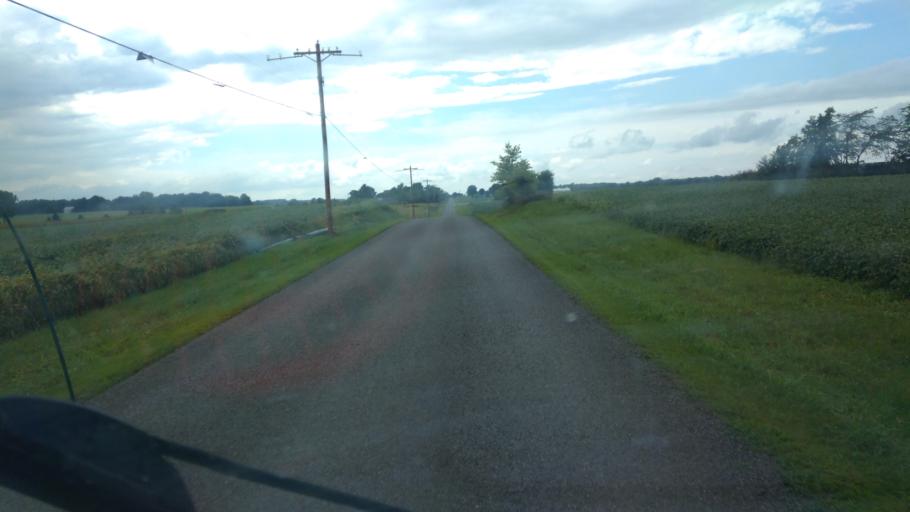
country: US
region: Ohio
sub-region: Hardin County
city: Kenton
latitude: 40.7038
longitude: -83.6278
